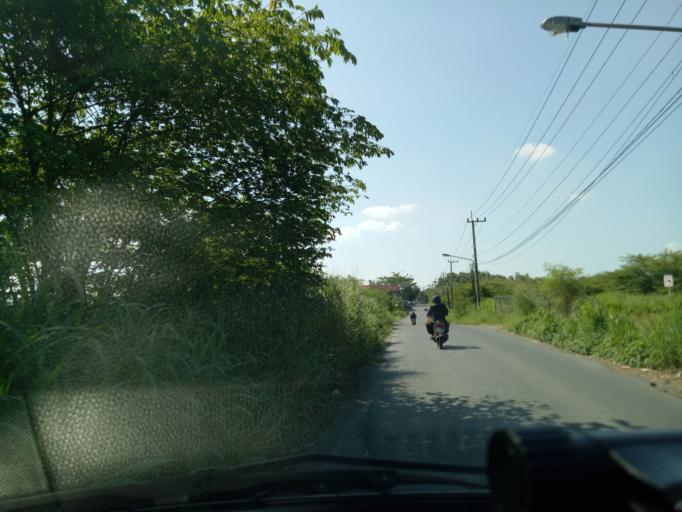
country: ID
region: East Java
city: Driyorejo
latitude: -7.2842
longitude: 112.6357
